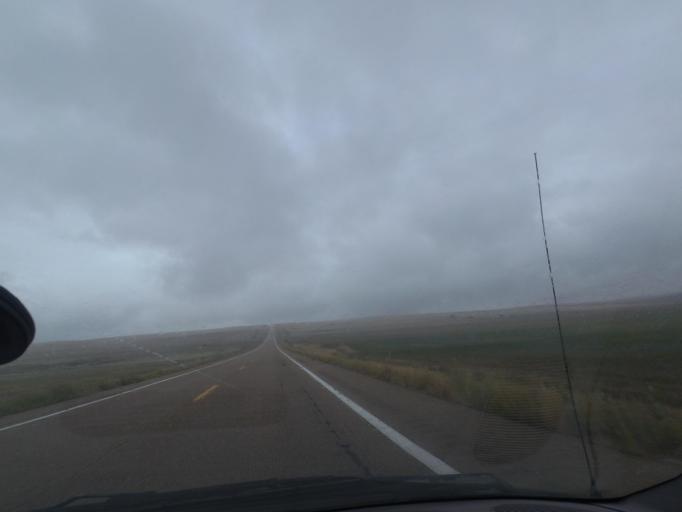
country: US
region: Colorado
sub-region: Arapahoe County
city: Byers
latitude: 39.7341
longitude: -103.8538
